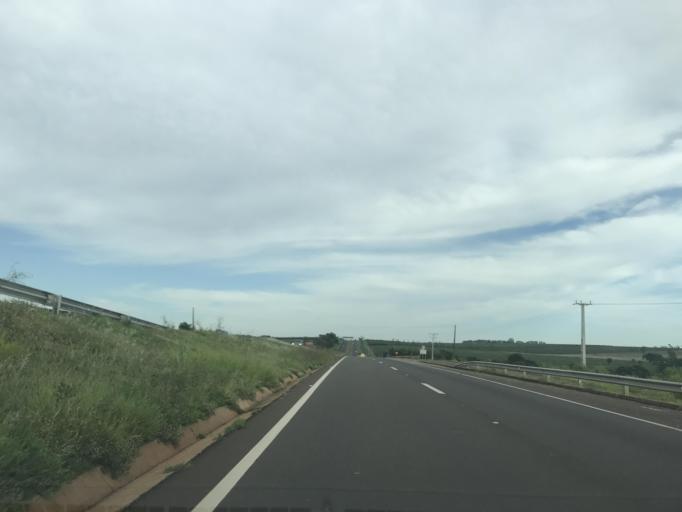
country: BR
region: Parana
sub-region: Alto Parana
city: Alto Parana
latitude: -23.1100
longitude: -52.3382
